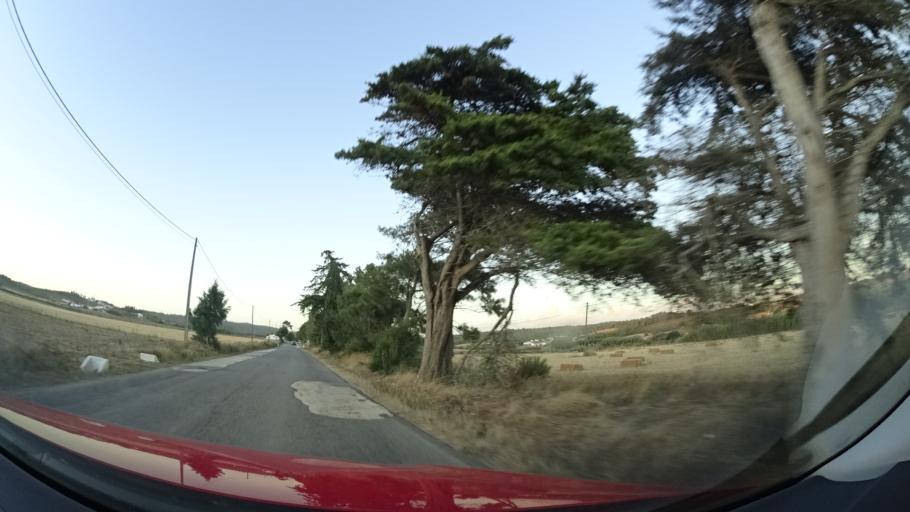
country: PT
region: Faro
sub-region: Aljezur
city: Aljezur
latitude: 37.2356
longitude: -8.8274
